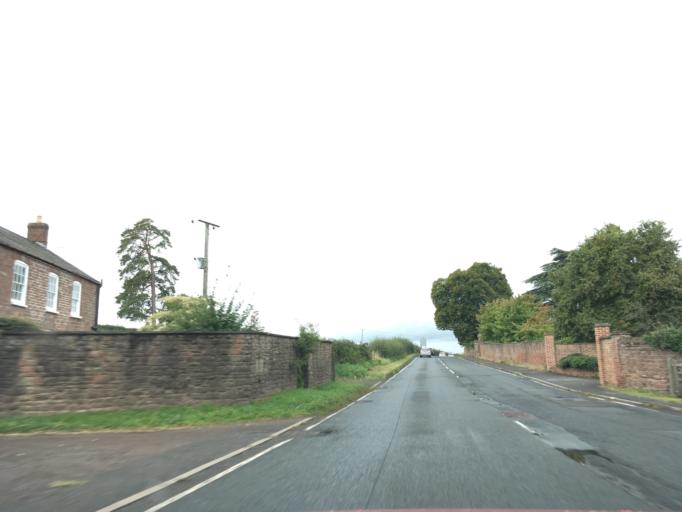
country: GB
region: England
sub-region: Herefordshire
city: Ross on Wye
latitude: 51.9094
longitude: -2.5435
